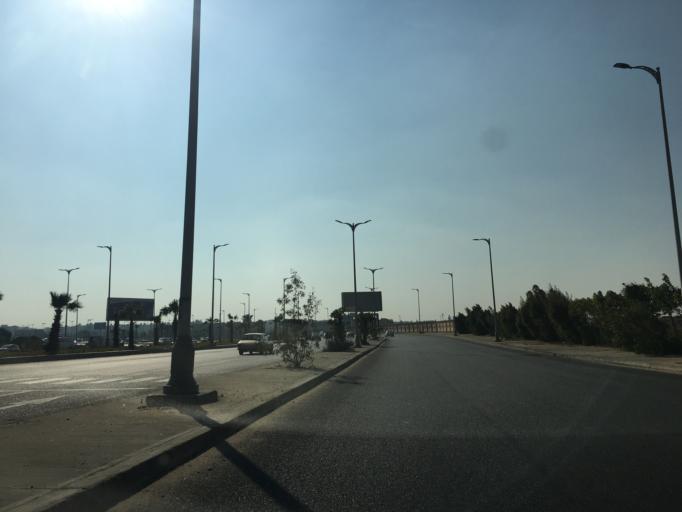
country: EG
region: Al Jizah
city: Madinat Sittah Uktubar
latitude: 29.9905
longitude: 30.9535
